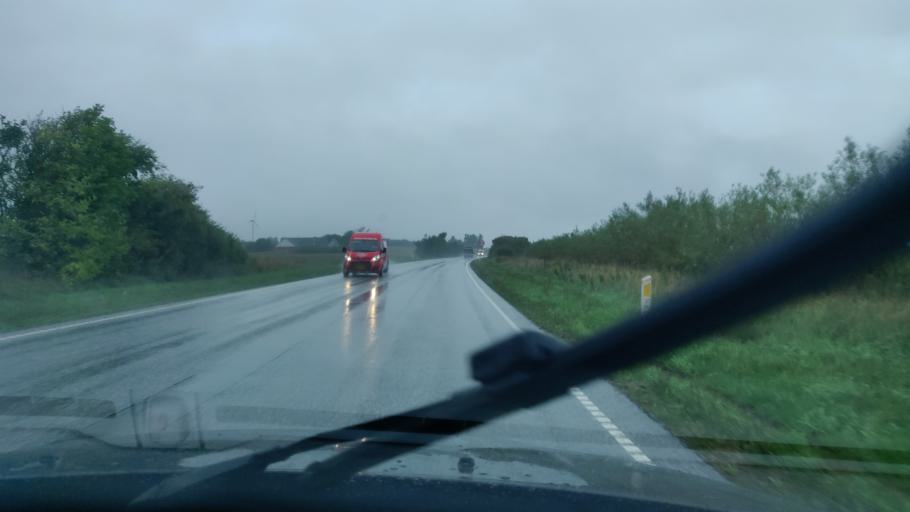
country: DK
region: North Denmark
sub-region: Thisted Kommune
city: Thisted
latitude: 56.9660
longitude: 8.6521
